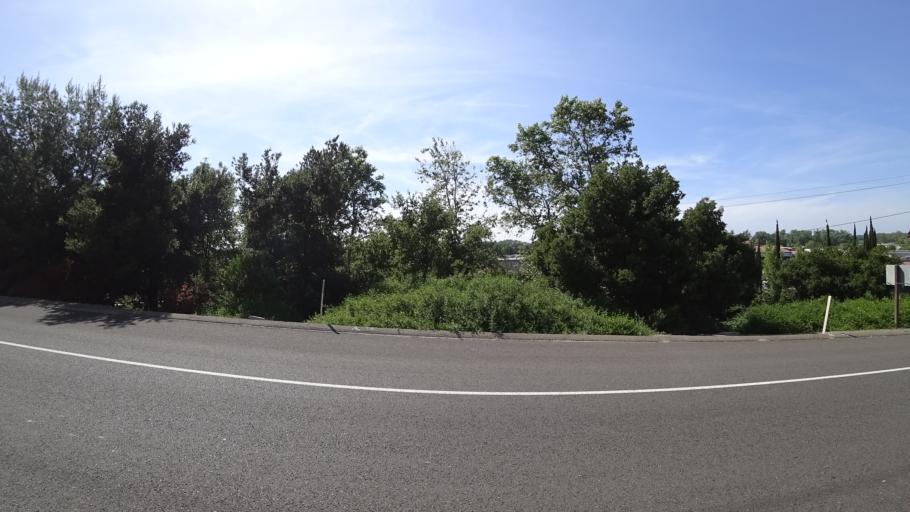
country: US
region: California
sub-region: Tehama County
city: Red Bluff
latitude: 40.1807
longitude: -122.2268
